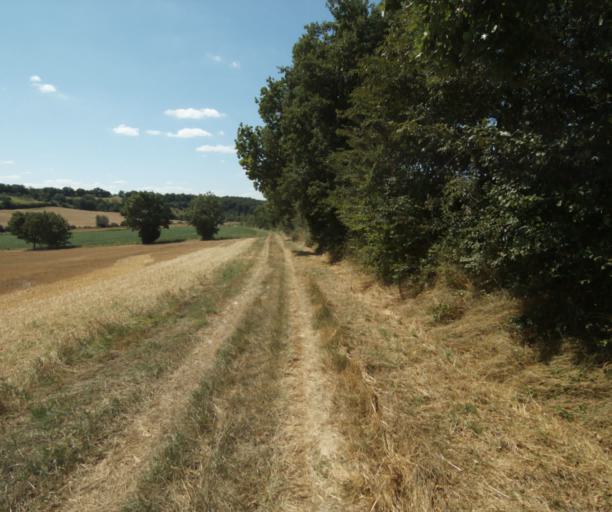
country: FR
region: Midi-Pyrenees
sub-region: Departement de la Haute-Garonne
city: Auriac-sur-Vendinelle
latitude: 43.5006
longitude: 1.8654
